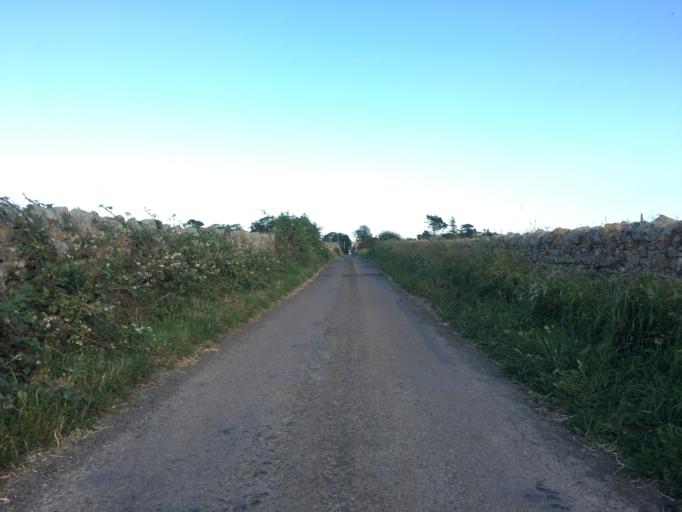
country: GB
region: England
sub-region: Northumberland
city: North Sunderland
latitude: 55.5886
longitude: -1.6815
